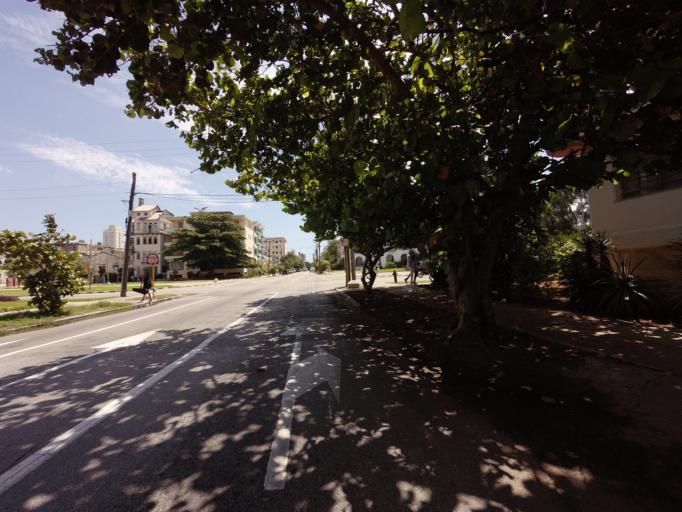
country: CU
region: La Habana
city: Havana
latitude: 23.1378
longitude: -82.4006
